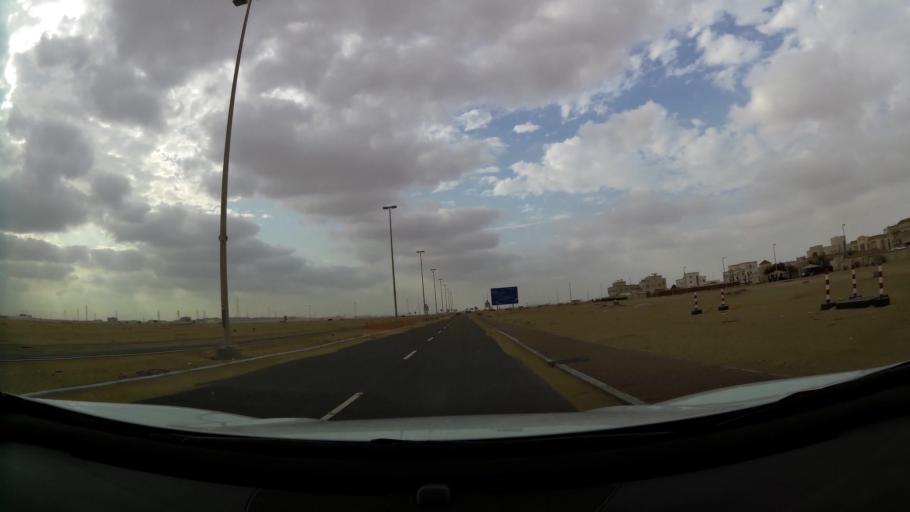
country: AE
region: Abu Dhabi
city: Abu Dhabi
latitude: 24.3466
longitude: 54.6090
